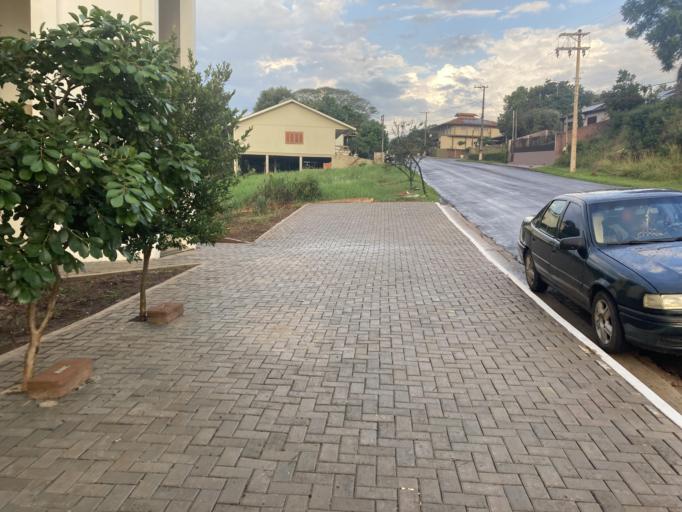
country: BR
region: Rio Grande do Sul
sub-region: Sao Pedro Do Butia
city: Butia Inferior
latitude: -27.9881
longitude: -54.8438
